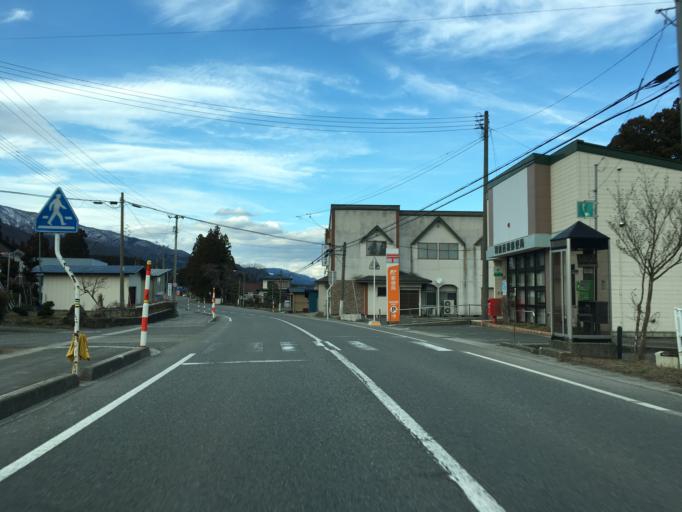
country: JP
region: Yamagata
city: Nagai
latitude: 38.1298
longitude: 140.0079
